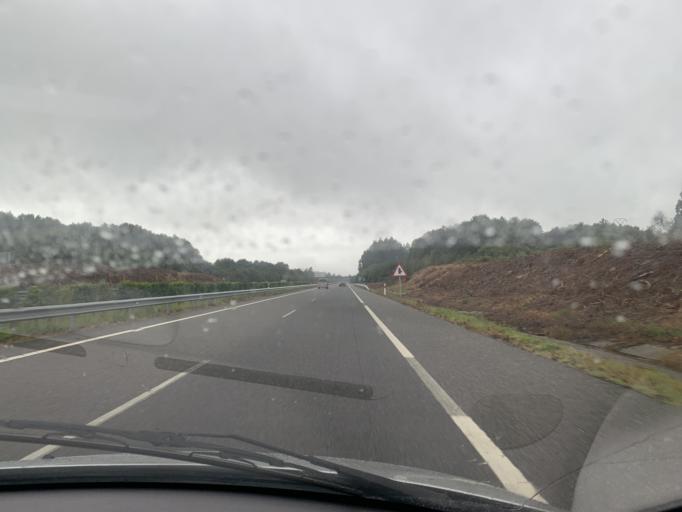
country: ES
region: Galicia
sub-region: Provincia de Lugo
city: Vilalba
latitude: 43.3255
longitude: -7.6228
